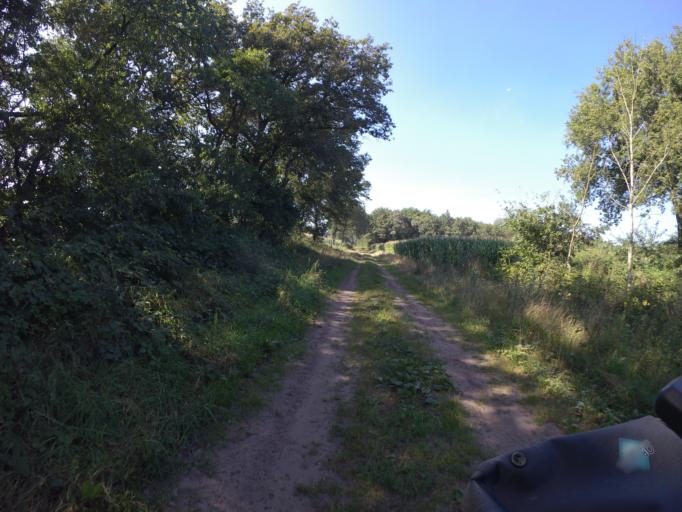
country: NL
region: North Brabant
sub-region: Gemeente Landerd
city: Zeeland
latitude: 51.6701
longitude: 5.6868
